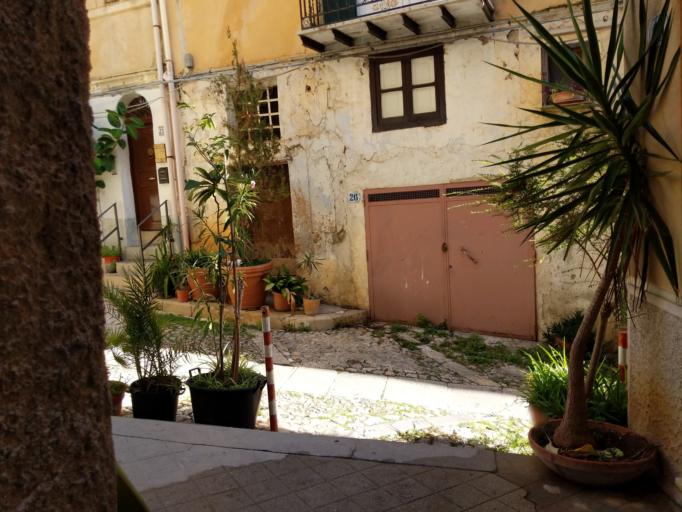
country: IT
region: Sicily
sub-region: Palermo
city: Monreale
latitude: 38.0824
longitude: 13.2933
